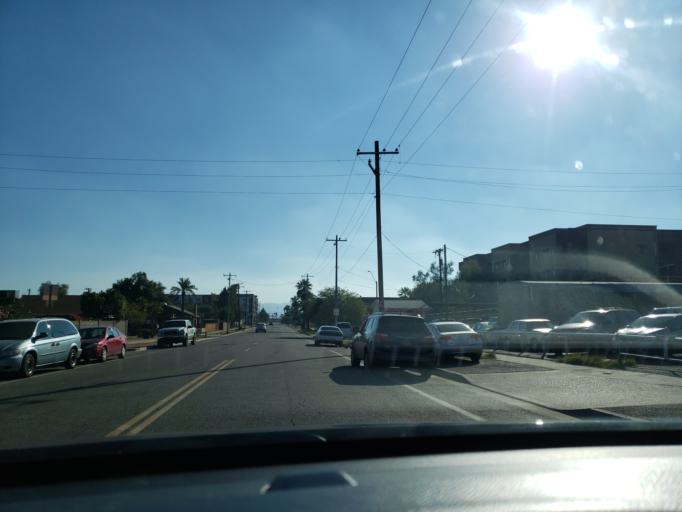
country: US
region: Arizona
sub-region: Maricopa County
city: Phoenix
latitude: 33.4512
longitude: -112.0564
